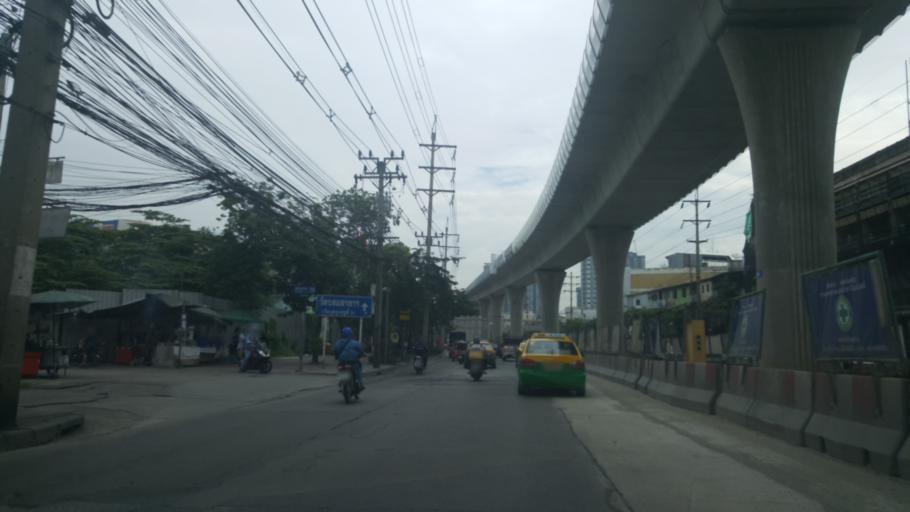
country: TH
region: Bangkok
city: Phasi Charoen
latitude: 13.7180
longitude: 100.4524
